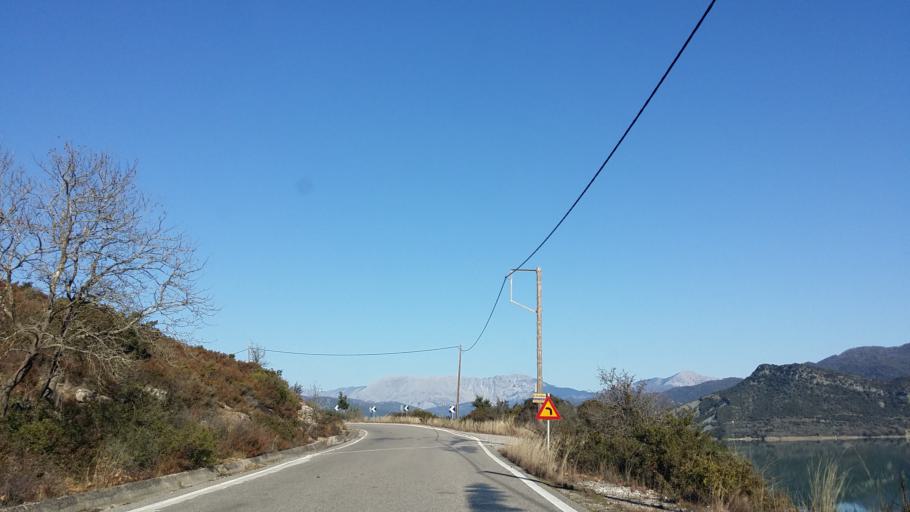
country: GR
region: West Greece
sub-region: Nomos Aitolias kai Akarnanias
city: Lepenou
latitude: 38.8173
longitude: 21.3347
